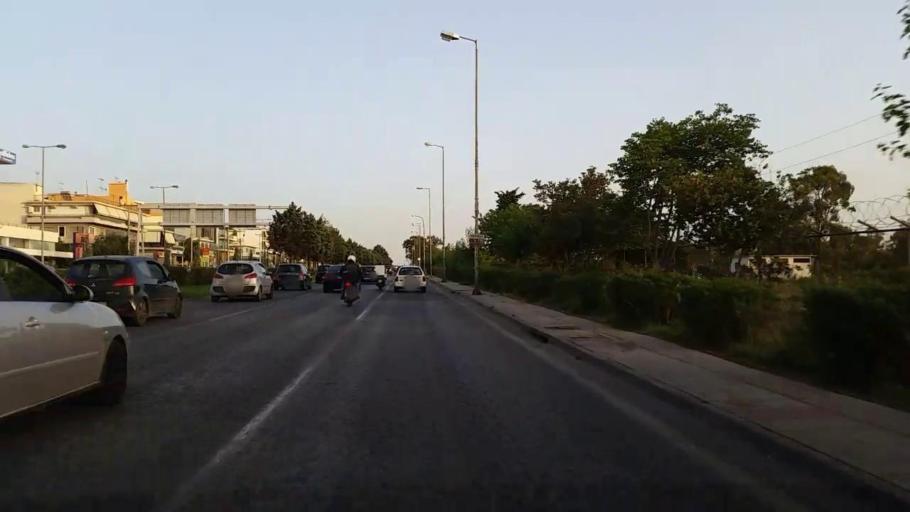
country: GR
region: Attica
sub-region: Nomarchia Athinas
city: Argyroupoli
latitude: 37.8998
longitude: 23.7462
